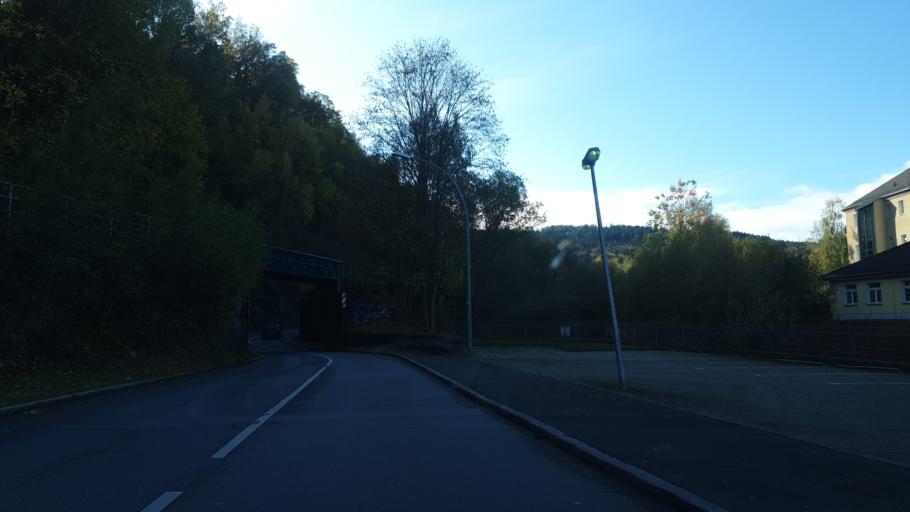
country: DE
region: Saxony
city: Aue
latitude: 50.5812
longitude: 12.6969
